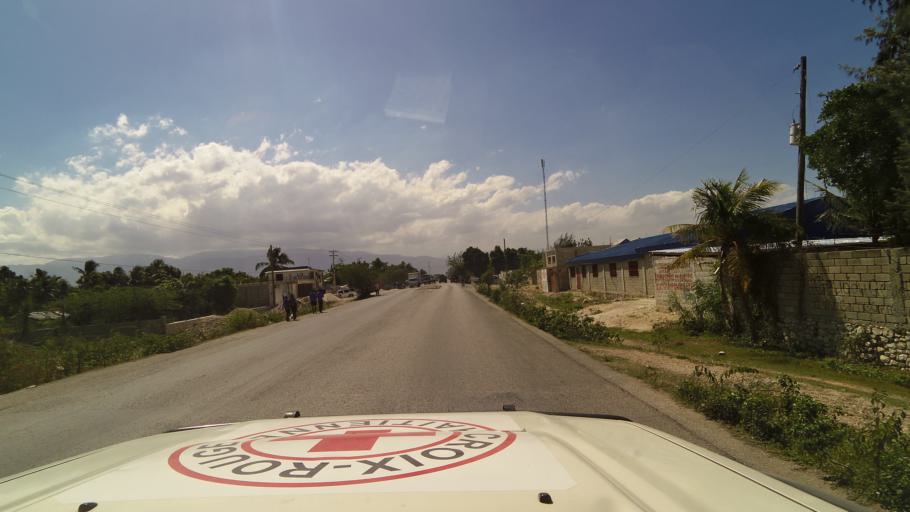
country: HT
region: Ouest
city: Delmas 73
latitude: 18.6156
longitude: -72.3151
